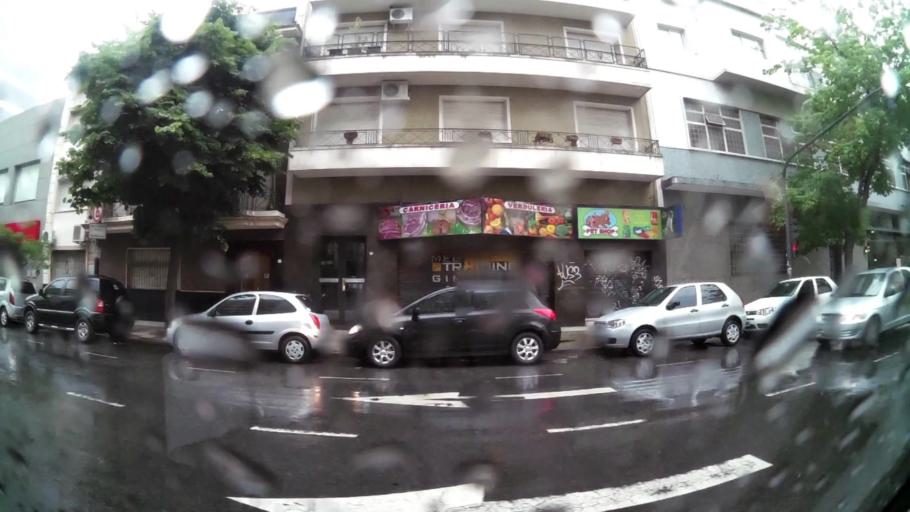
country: AR
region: Buenos Aires F.D.
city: Buenos Aires
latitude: -34.6319
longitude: -58.3731
